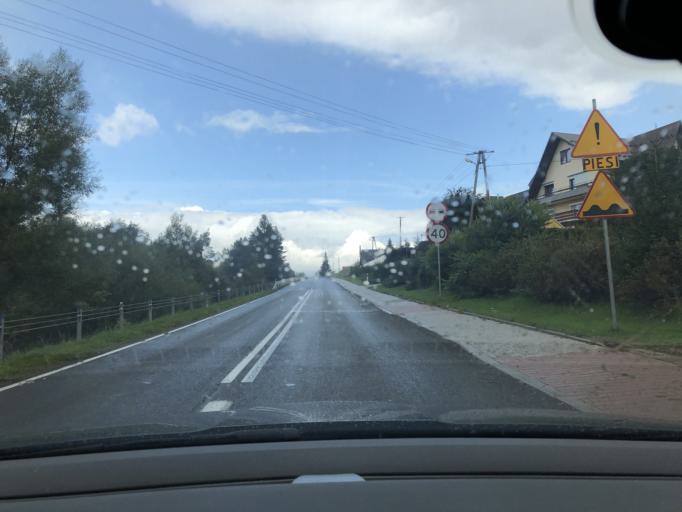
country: PL
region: Lesser Poland Voivodeship
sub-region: Powiat nowotarski
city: Zubrzyca Dolna
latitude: 49.5141
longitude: 19.6740
